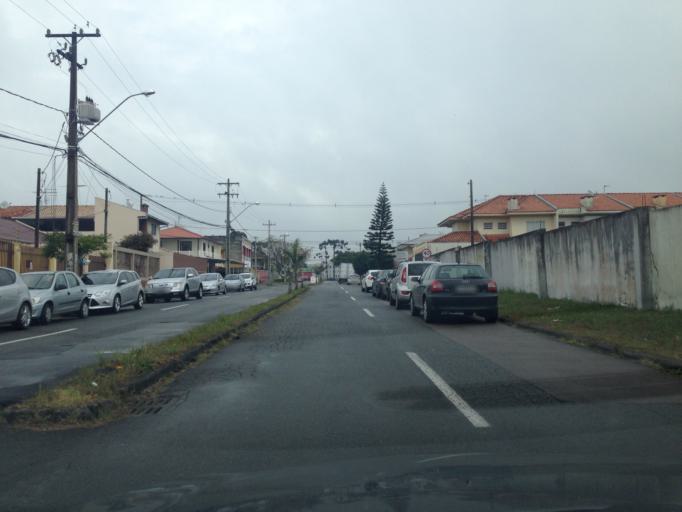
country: BR
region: Parana
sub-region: Sao Jose Dos Pinhais
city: Sao Jose dos Pinhais
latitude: -25.5543
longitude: -49.1691
